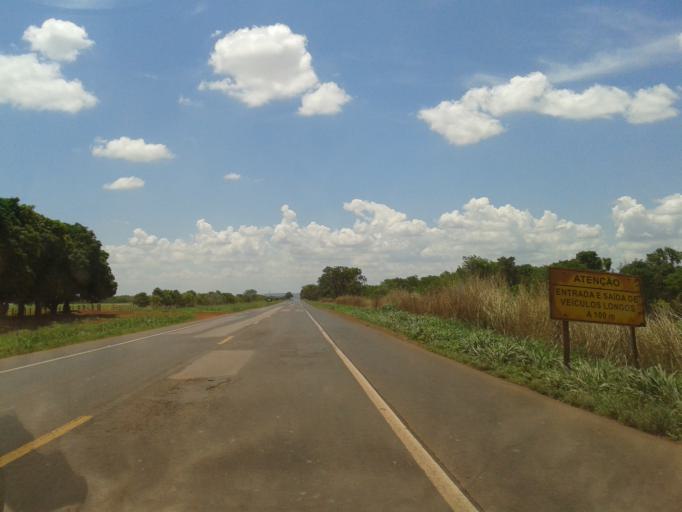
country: BR
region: Goias
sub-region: Goiatuba
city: Goiatuba
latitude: -18.2707
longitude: -49.6443
